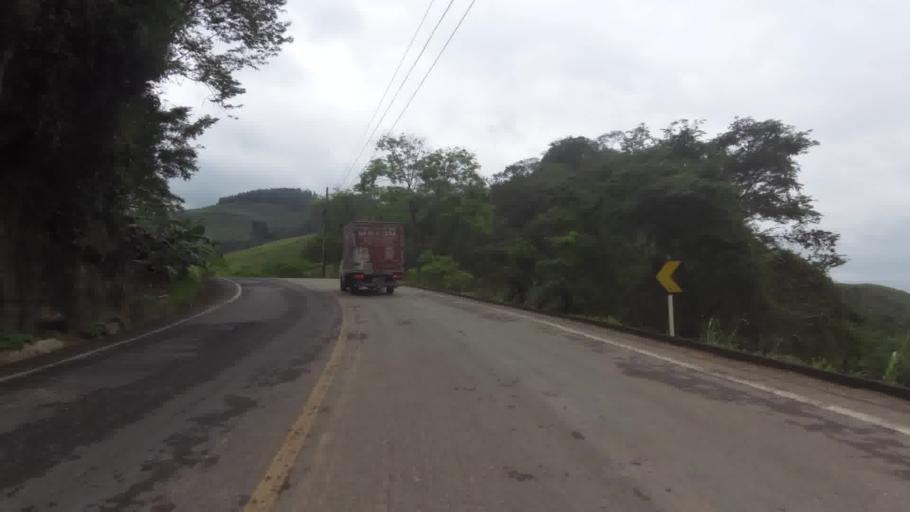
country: BR
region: Espirito Santo
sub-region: Iconha
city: Iconha
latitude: -20.7546
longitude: -40.8368
